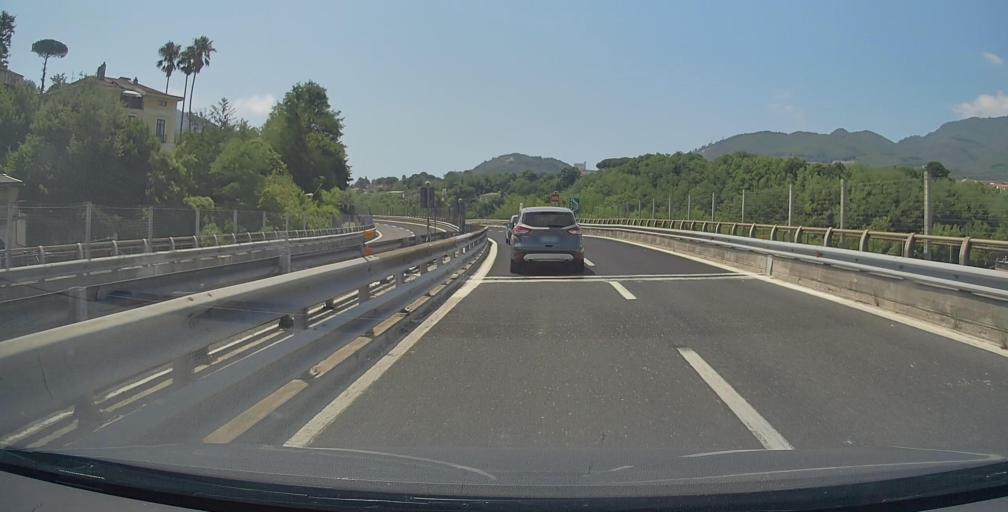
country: IT
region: Campania
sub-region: Provincia di Salerno
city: Cava De Tirreni
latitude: 40.6949
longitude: 14.7148
